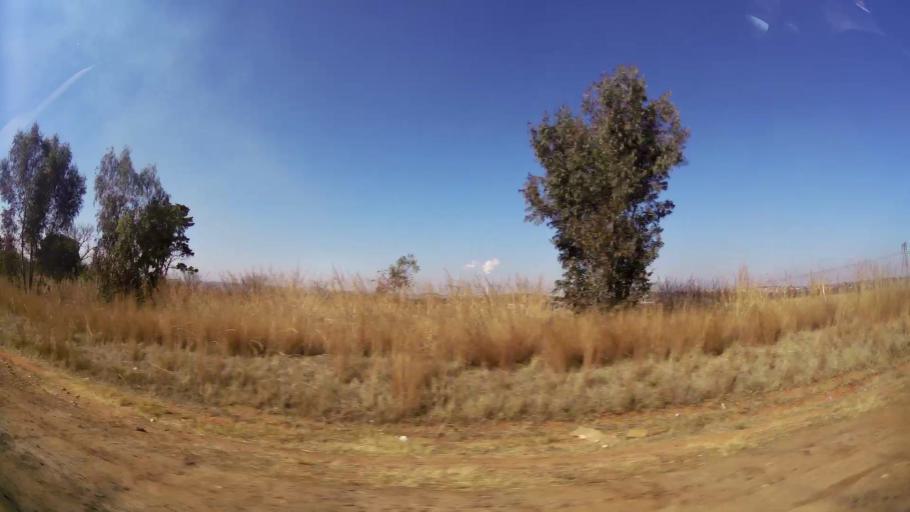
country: ZA
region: Mpumalanga
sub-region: Nkangala District Municipality
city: Witbank
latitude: -25.8362
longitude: 29.2500
